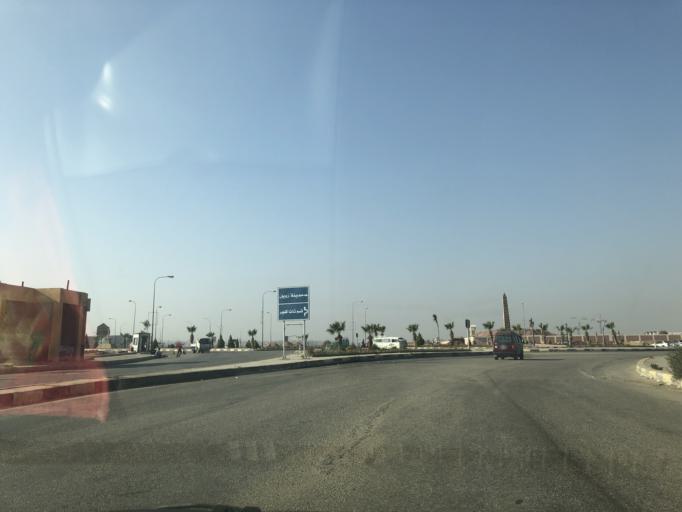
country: EG
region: Al Jizah
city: Madinat Sittah Uktubar
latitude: 29.9324
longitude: 31.0447
